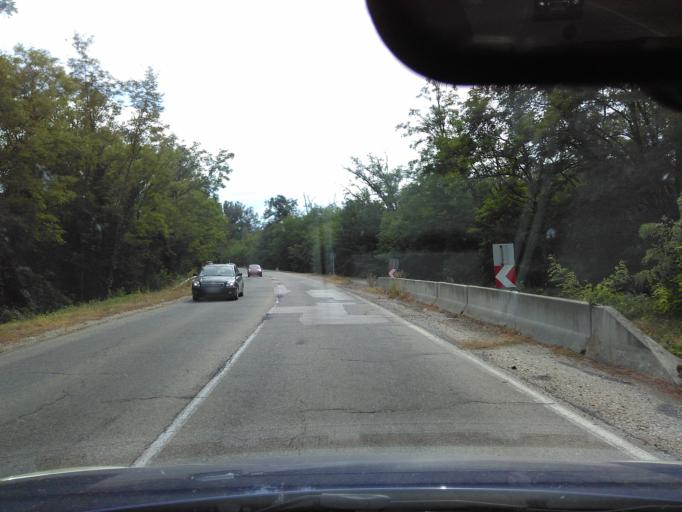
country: HU
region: Pest
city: Domony
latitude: 47.6173
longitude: 19.4082
